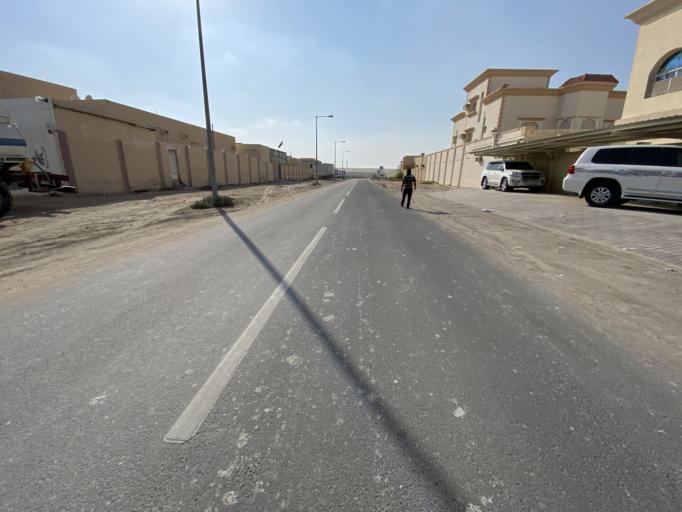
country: QA
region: Baladiyat ar Rayyan
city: Ar Rayyan
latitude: 25.2326
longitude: 51.3770
